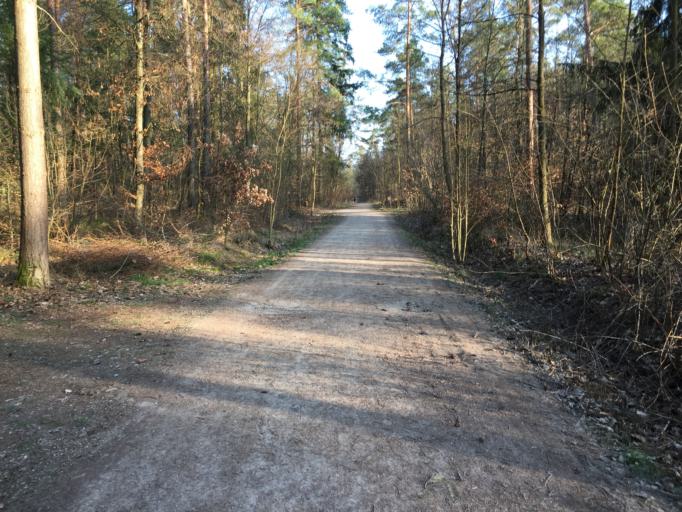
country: DE
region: Bavaria
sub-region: Regierungsbezirk Mittelfranken
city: Buckenhof
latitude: 49.5586
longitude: 11.0360
